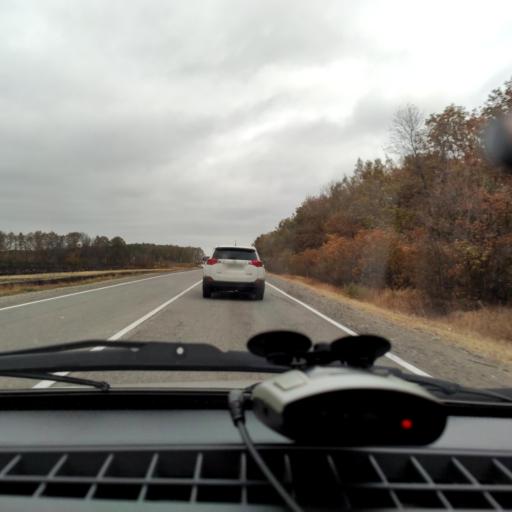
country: RU
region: Voronezj
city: Shilovo
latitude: 51.4238
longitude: 39.0084
